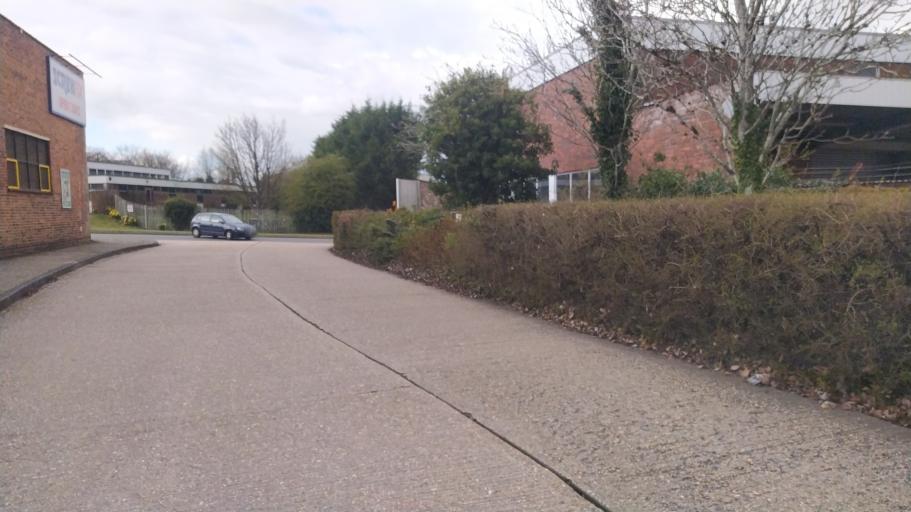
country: GB
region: England
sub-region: Hampshire
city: Andover
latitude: 51.2119
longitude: -1.5100
